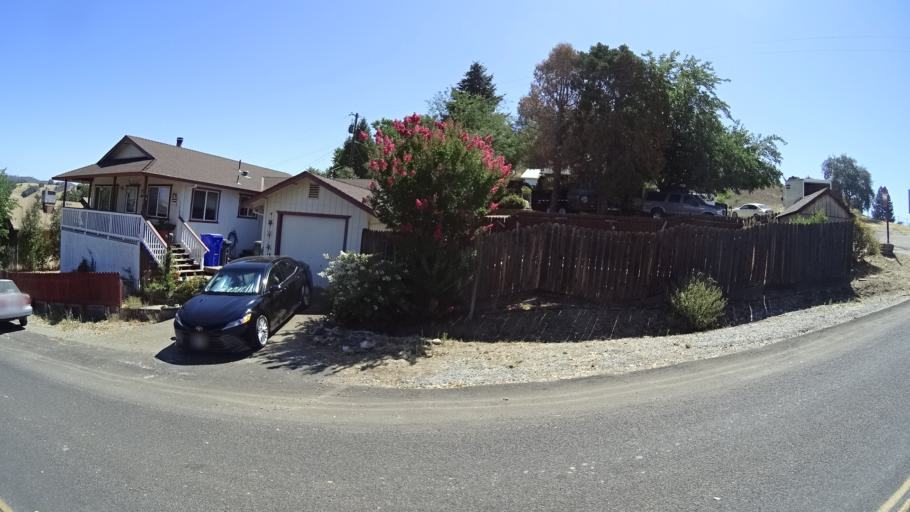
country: US
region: California
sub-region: Calaveras County
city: San Andreas
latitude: 38.1942
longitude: -120.6814
